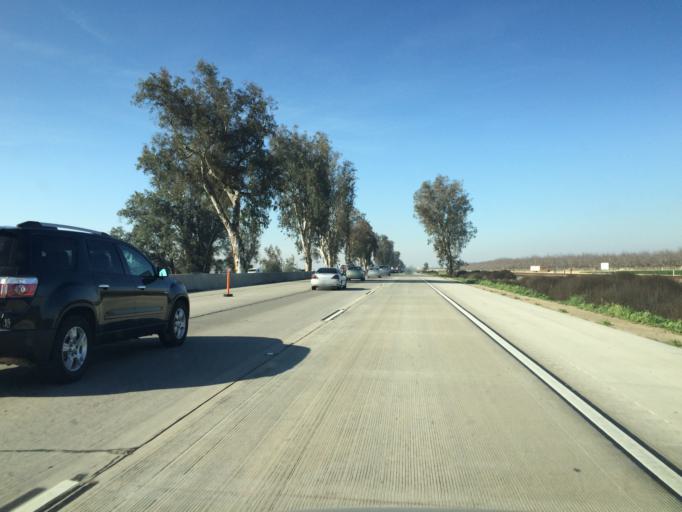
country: US
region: California
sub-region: Tulare County
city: Goshen
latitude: 36.3686
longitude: -119.4327
